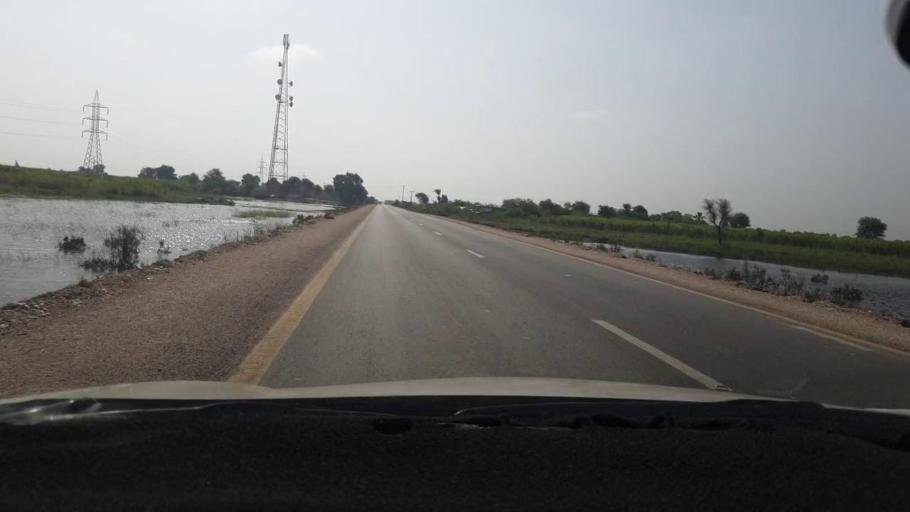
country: PK
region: Sindh
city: Jhol
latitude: 25.8768
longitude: 69.0428
